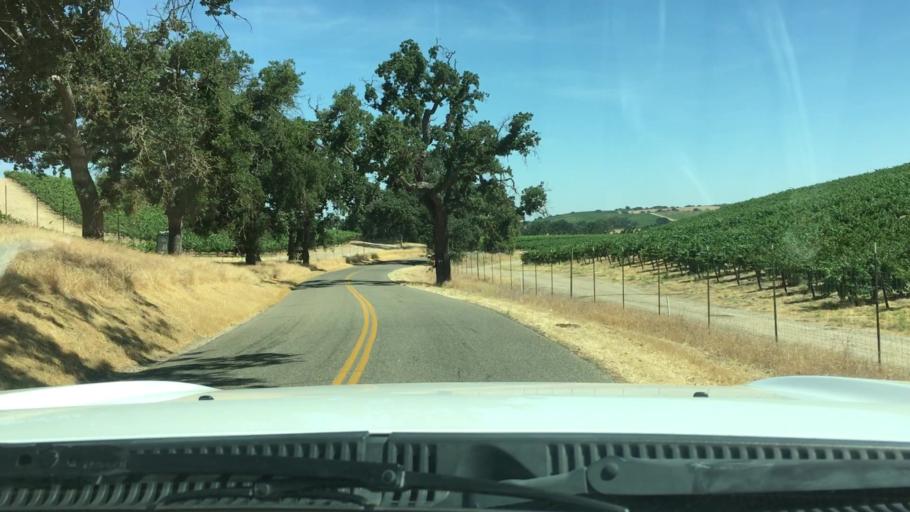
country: US
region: California
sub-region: San Luis Obispo County
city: Atascadero
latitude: 35.5635
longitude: -120.6070
